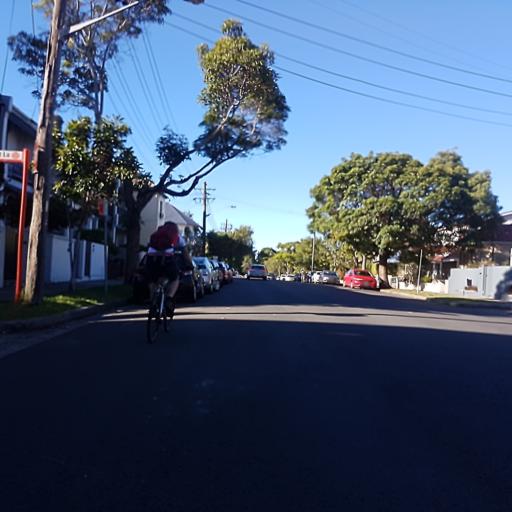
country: AU
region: New South Wales
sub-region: North Sydney
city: Crows Nest
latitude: -33.8262
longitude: 151.2069
